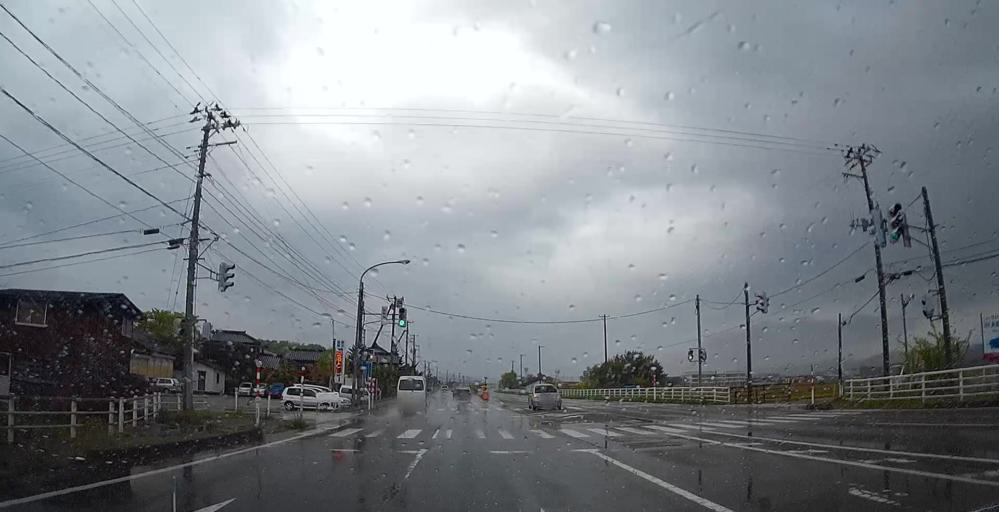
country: JP
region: Niigata
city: Kashiwazaki
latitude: 37.4183
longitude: 138.6169
